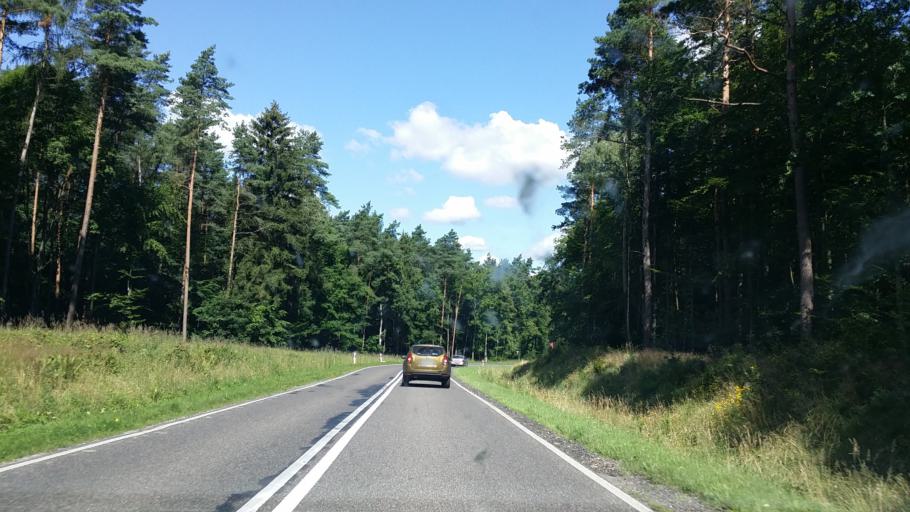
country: PL
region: West Pomeranian Voivodeship
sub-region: Powiat drawski
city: Drawsko Pomorskie
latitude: 53.4770
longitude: 15.8152
